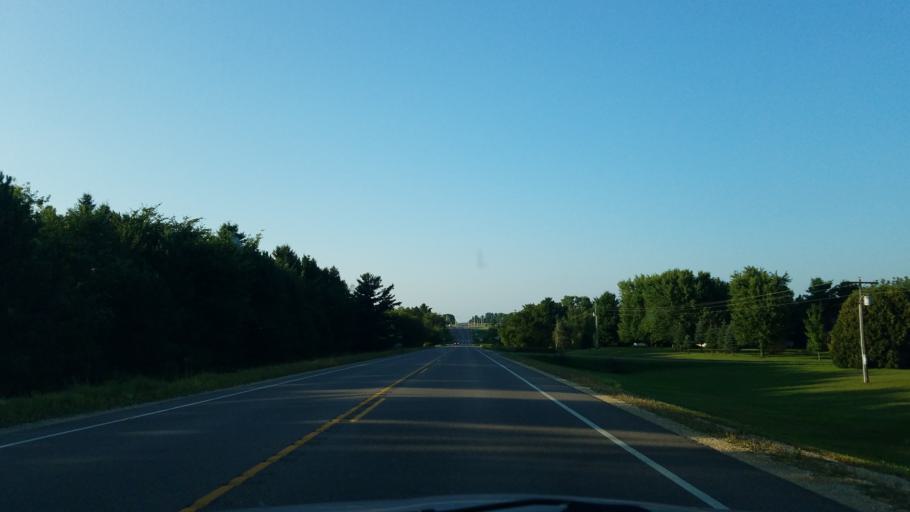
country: US
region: Wisconsin
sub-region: Saint Croix County
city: New Richmond
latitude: 45.1297
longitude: -92.3838
